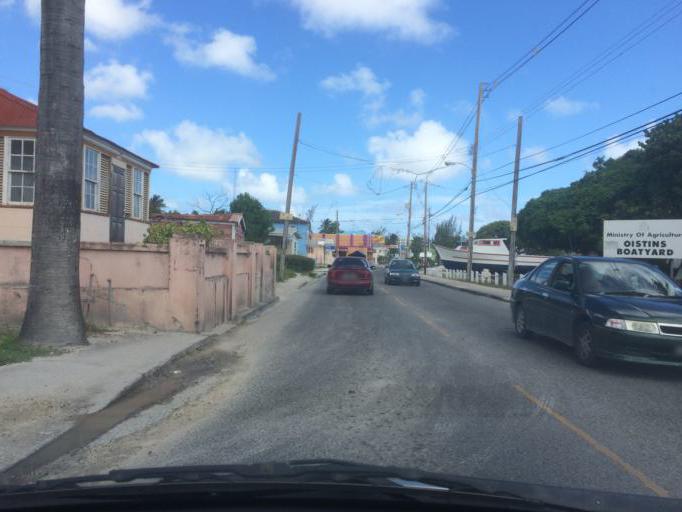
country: BB
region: Christ Church
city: Oistins
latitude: 13.0645
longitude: -59.5451
